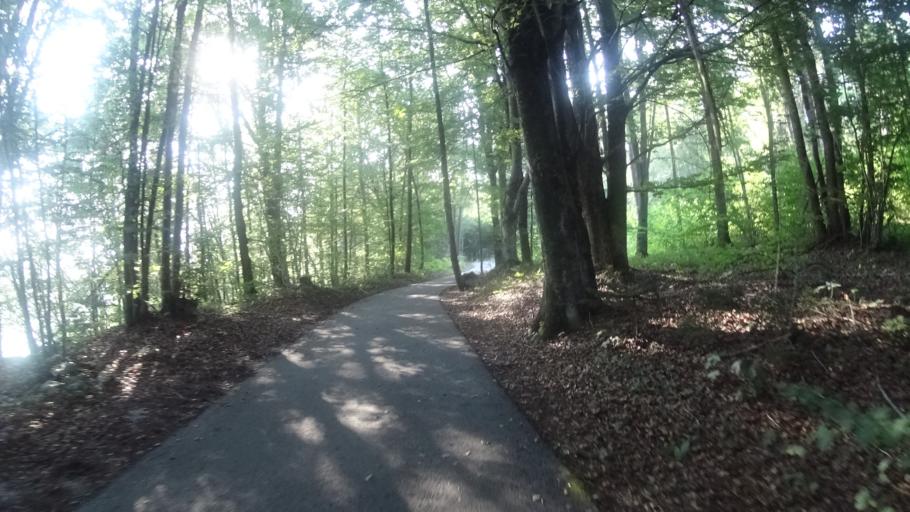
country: AT
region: Carinthia
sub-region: Politischer Bezirk Klagenfurt Land
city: Ludmannsdorf
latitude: 46.5334
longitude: 14.1183
